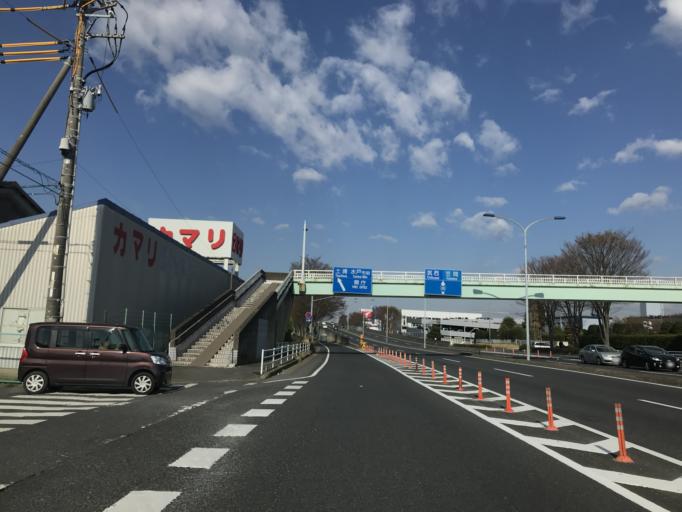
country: JP
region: Ibaraki
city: Mito-shi
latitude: 36.3466
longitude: 140.4685
